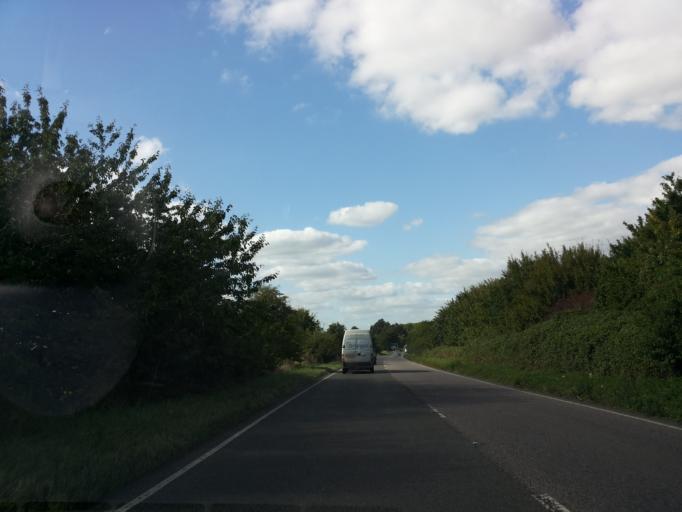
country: GB
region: England
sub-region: Wiltshire
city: Chapmanslade
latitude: 51.2284
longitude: -2.2266
